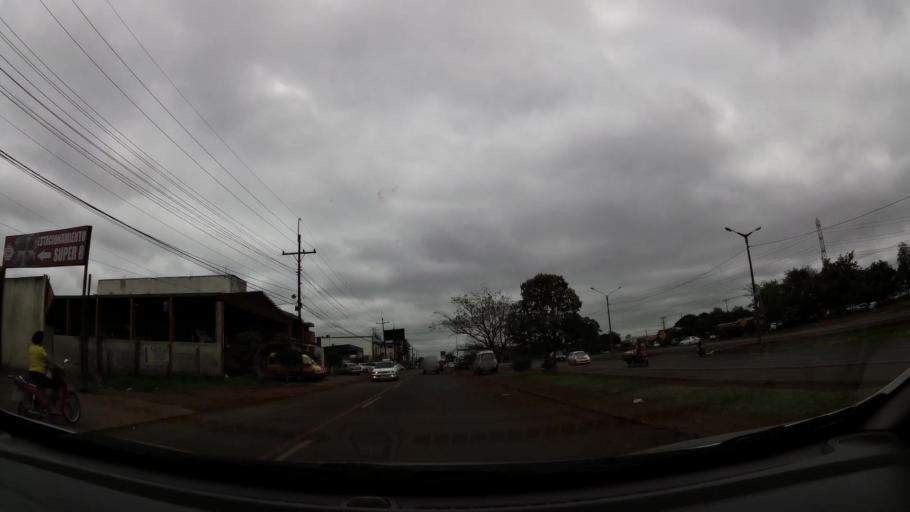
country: PY
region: Alto Parana
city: Ciudad del Este
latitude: -25.4963
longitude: -54.6839
